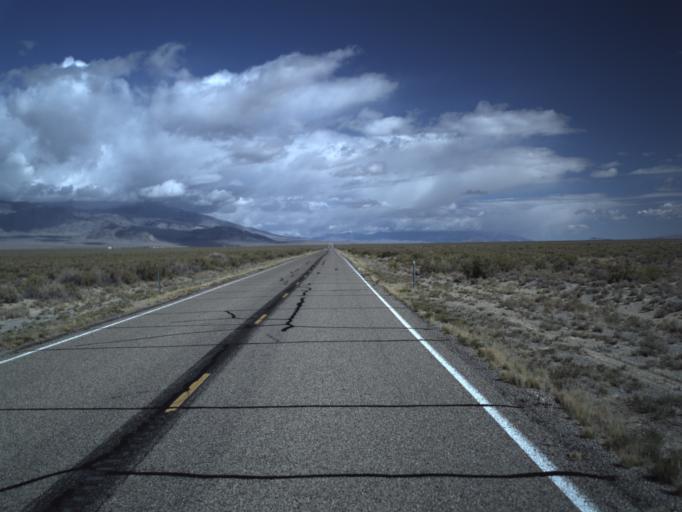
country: US
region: Nevada
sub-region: White Pine County
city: McGill
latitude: 39.0080
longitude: -114.0350
